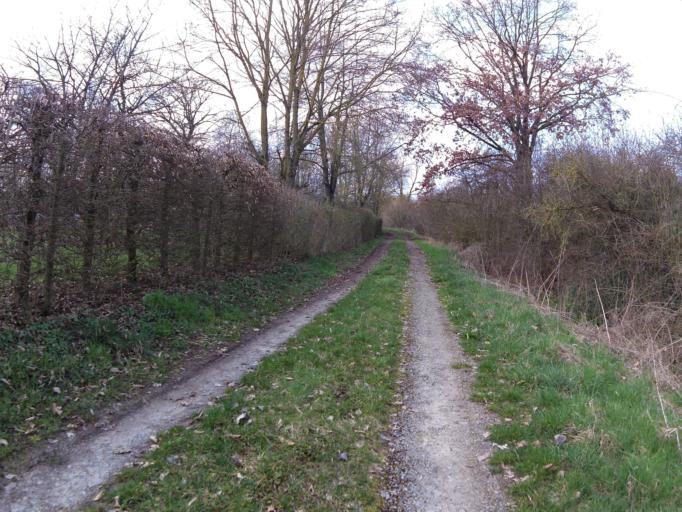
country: DE
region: Bavaria
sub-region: Regierungsbezirk Unterfranken
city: Buchbrunn
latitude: 49.7522
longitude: 10.1138
